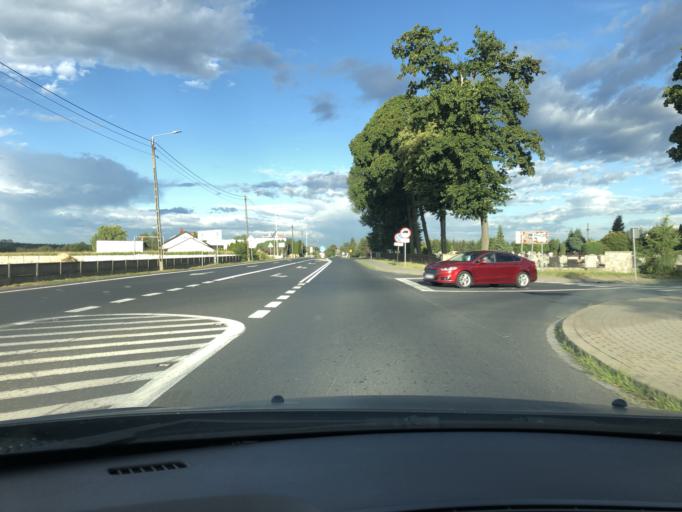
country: PL
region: Lodz Voivodeship
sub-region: Powiat wieruszowski
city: Sokolniki
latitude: 51.3048
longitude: 18.3168
